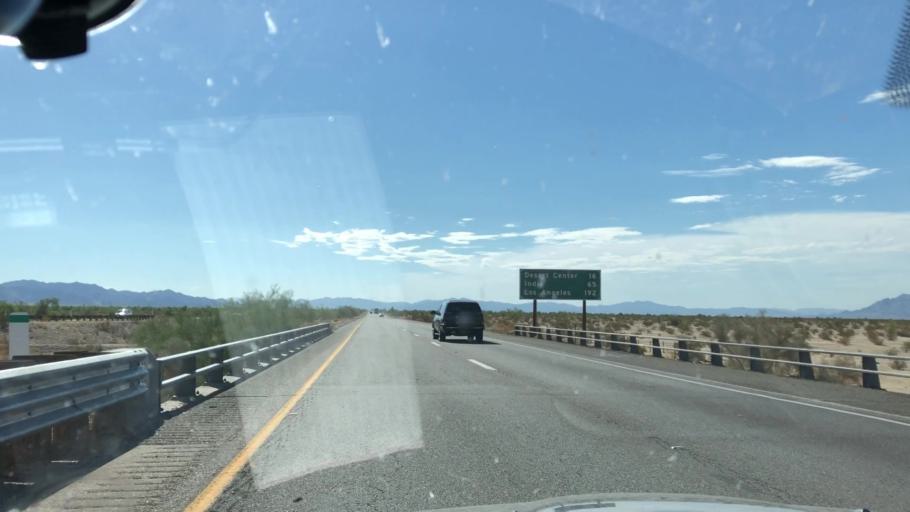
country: US
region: California
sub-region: Riverside County
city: Mesa Verde
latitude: 33.6518
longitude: -115.1393
